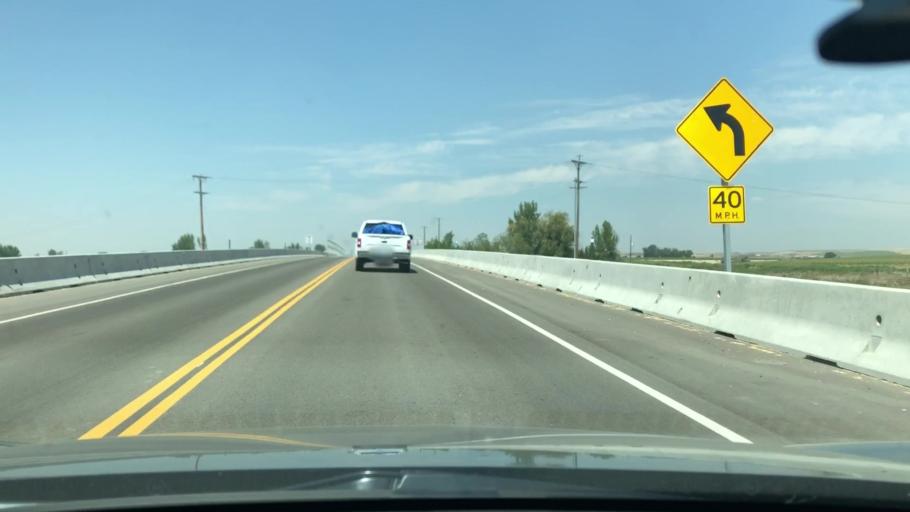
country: US
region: Idaho
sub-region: Canyon County
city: Parma
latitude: 43.7650
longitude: -116.9117
